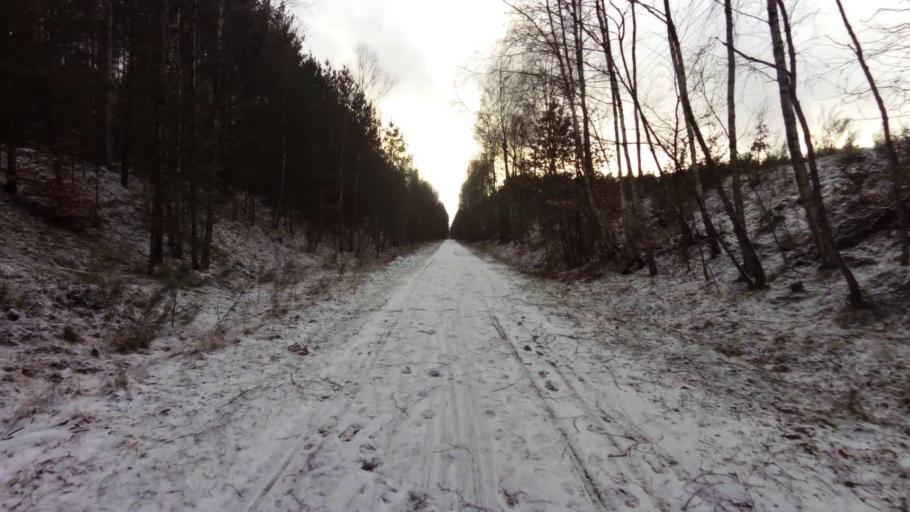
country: PL
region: West Pomeranian Voivodeship
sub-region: Powiat drawski
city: Zlocieniec
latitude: 53.5613
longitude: 16.0330
